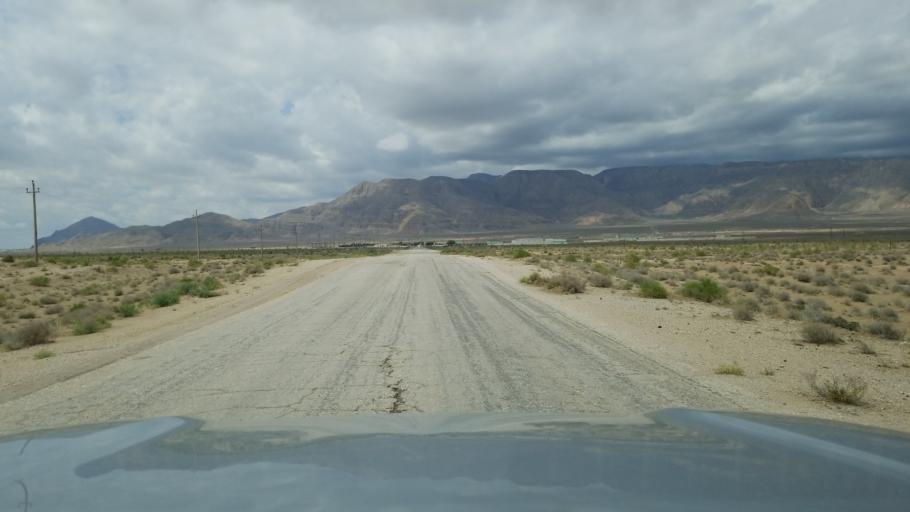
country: TM
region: Balkan
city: Balkanabat
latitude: 39.4670
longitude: 54.4660
